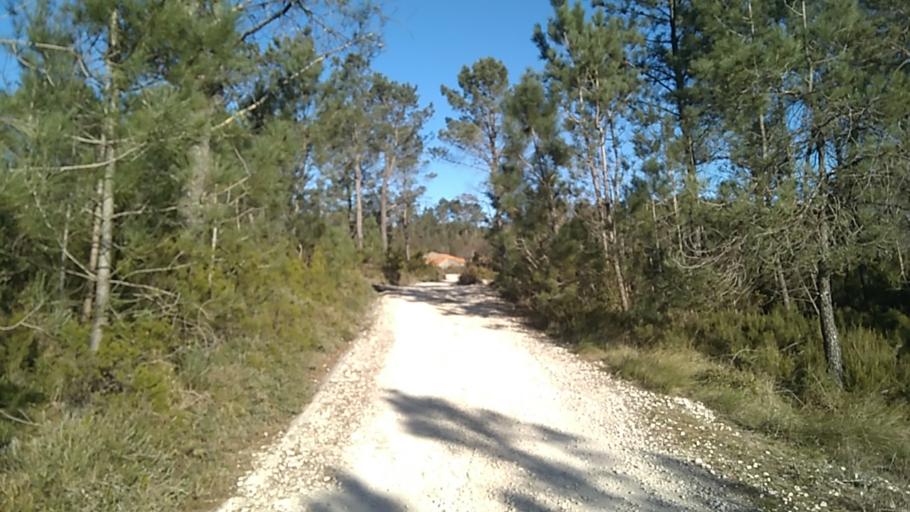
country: PT
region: Leiria
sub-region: Porto de Mos
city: Porto de Mos
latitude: 39.5353
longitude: -8.8583
